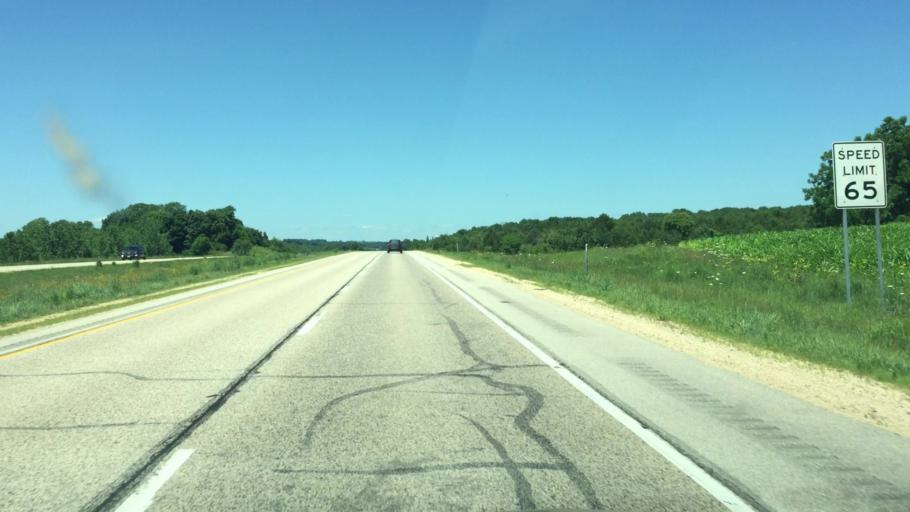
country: US
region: Iowa
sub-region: Jackson County
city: Maquoketa
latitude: 42.1364
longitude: -90.6777
